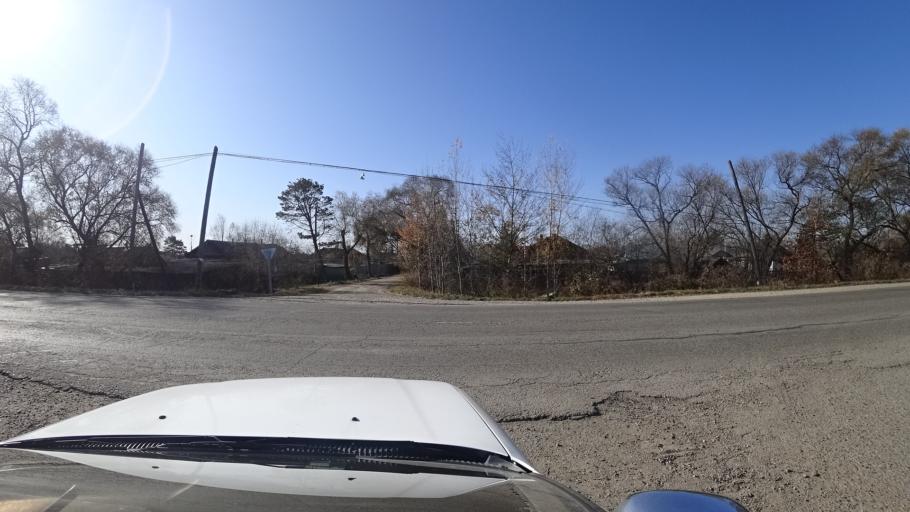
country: RU
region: Primorskiy
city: Dal'nerechensk
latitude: 45.9102
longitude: 133.8042
